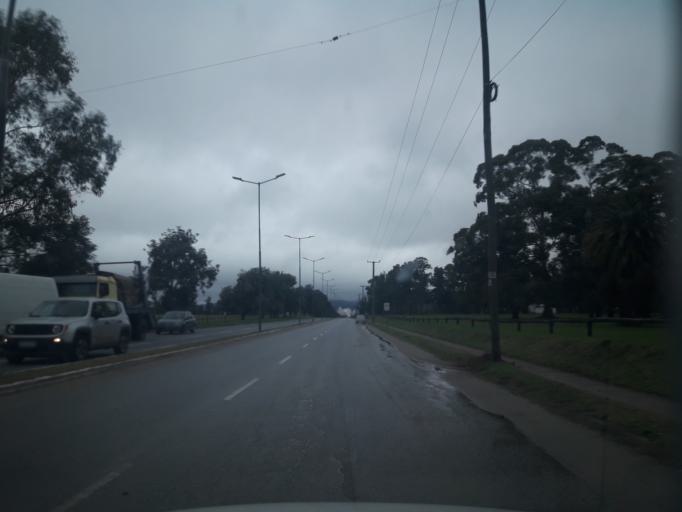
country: AR
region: Buenos Aires
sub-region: Partido de Tandil
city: Tandil
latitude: -37.3051
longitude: -59.1645
